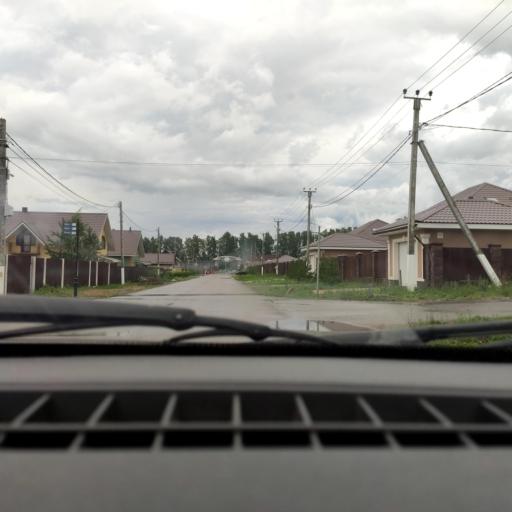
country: RU
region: Bashkortostan
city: Kabakovo
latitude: 54.5966
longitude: 56.2076
